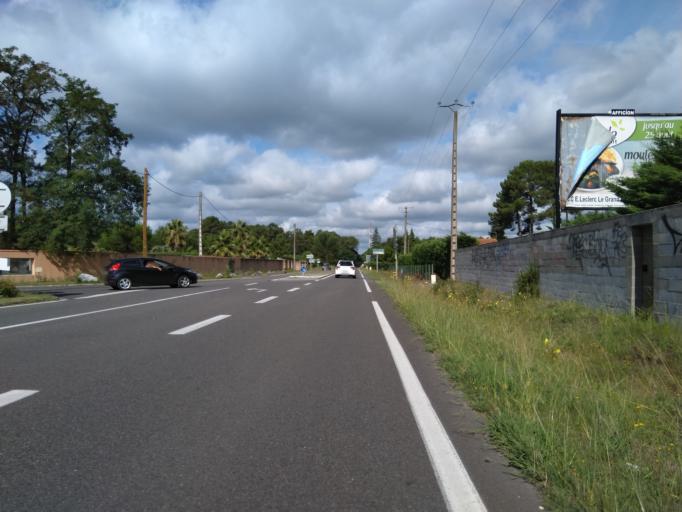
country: FR
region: Aquitaine
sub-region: Departement des Landes
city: Mees
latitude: 43.7319
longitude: -1.0994
